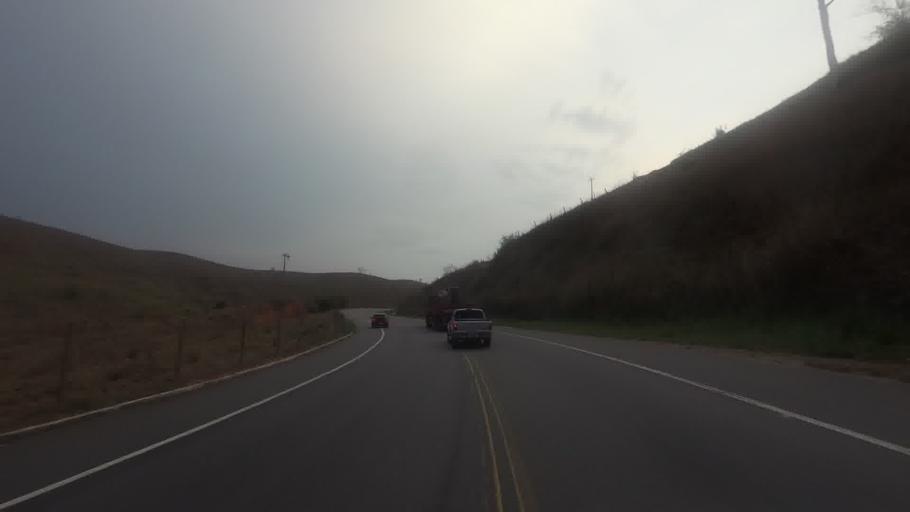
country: BR
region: Rio de Janeiro
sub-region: Carmo
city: Carmo
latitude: -21.8106
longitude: -42.5934
